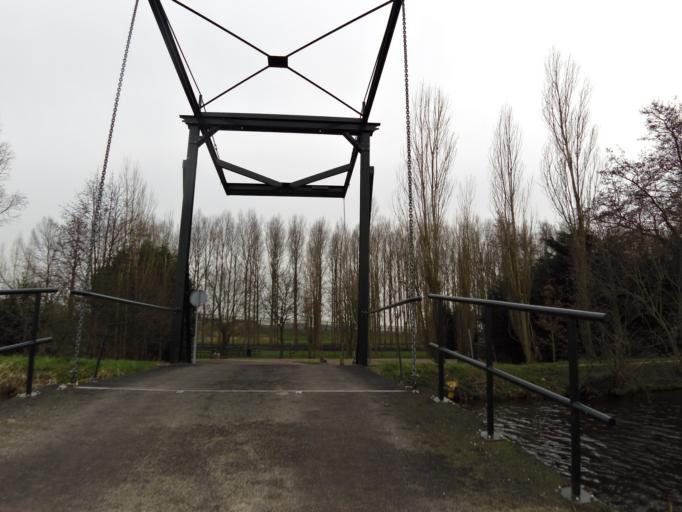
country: NL
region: South Holland
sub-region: Gemeente Leiderdorp
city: Leiderdorp
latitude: 52.1684
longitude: 4.5604
